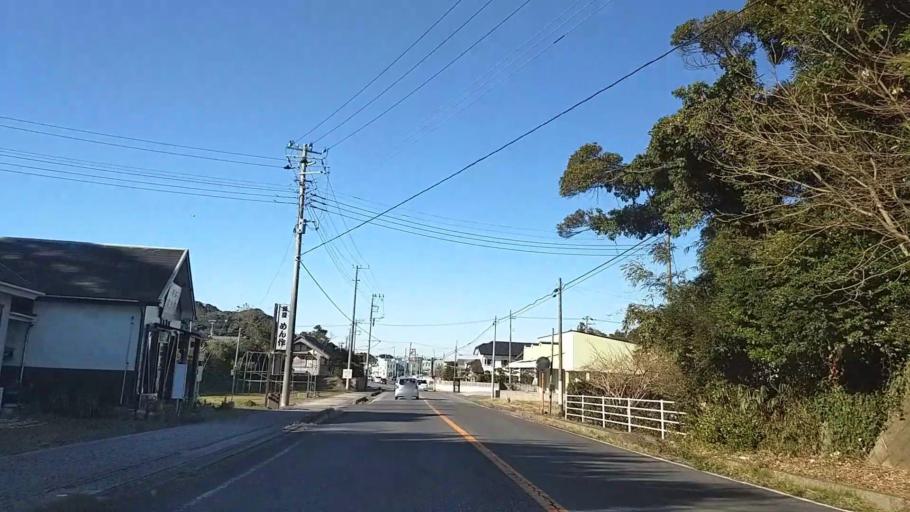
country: JP
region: Chiba
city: Ohara
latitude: 35.3237
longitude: 140.4016
